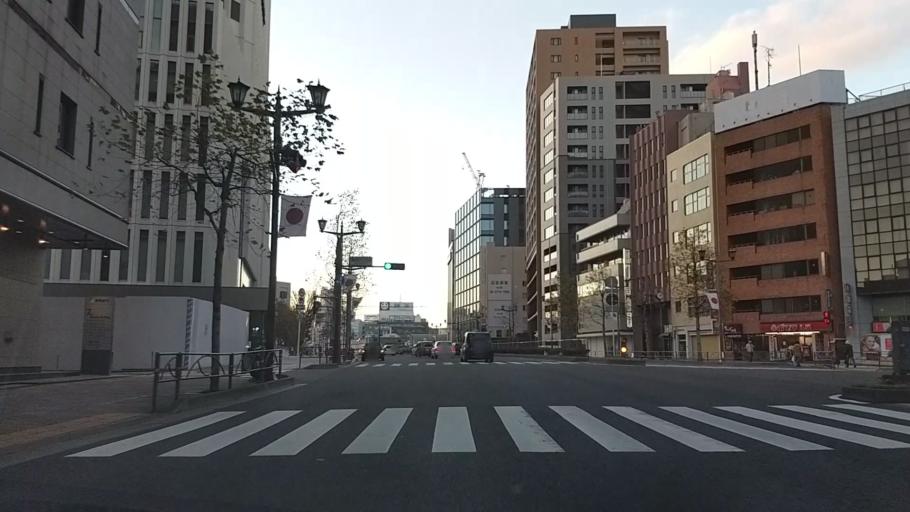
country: JP
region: Tokyo
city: Tokyo
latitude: 35.6846
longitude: 139.7337
